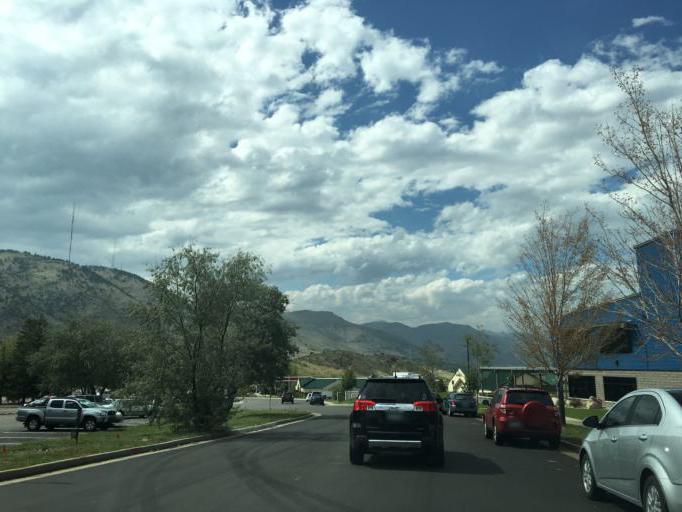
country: US
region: Colorado
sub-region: Jefferson County
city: West Pleasant View
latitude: 39.7274
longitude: -105.2070
